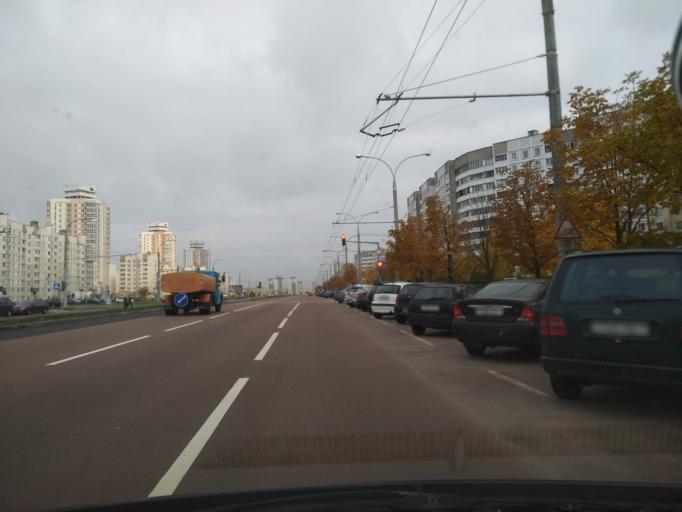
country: BY
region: Minsk
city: Novoye Medvezhino
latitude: 53.9091
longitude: 27.4361
